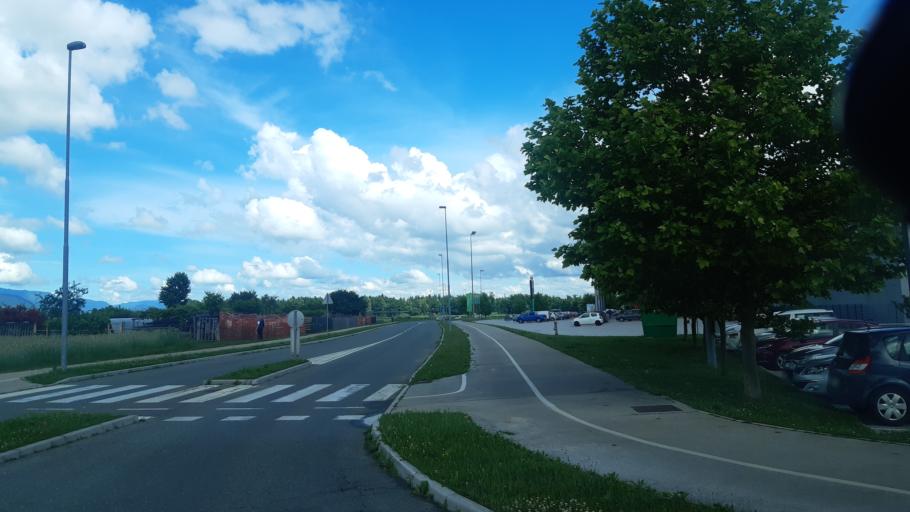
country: SI
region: Kranj
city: Kranj
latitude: 46.2376
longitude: 14.3722
